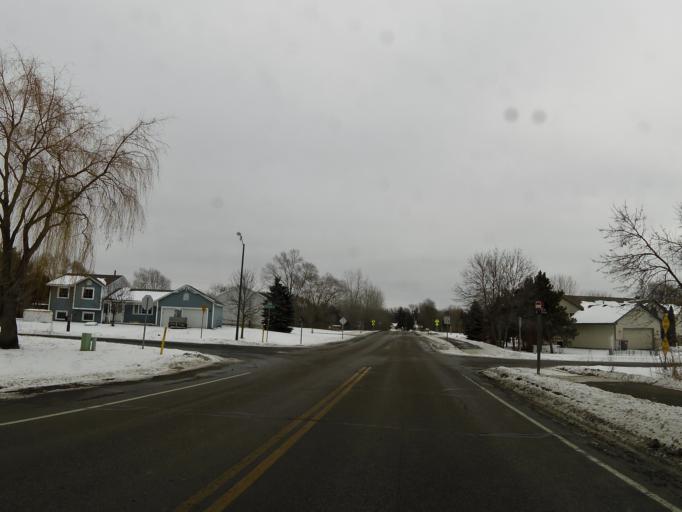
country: US
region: Minnesota
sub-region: Ramsey County
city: Little Canada
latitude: 45.0080
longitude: -93.0449
